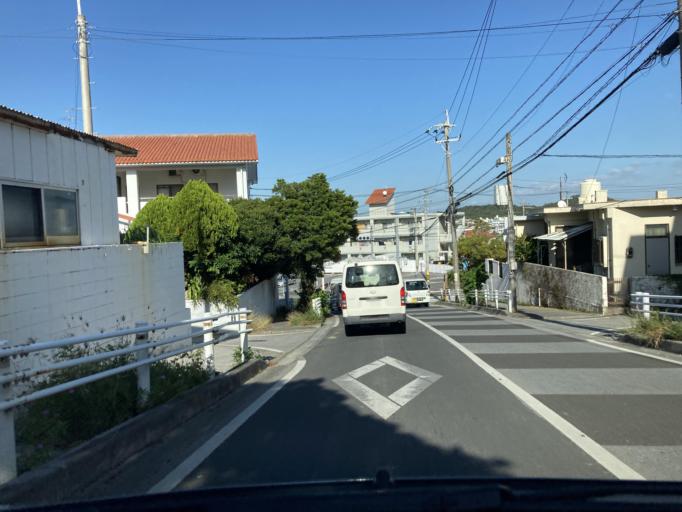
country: JP
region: Okinawa
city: Tomigusuku
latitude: 26.1796
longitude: 127.7065
